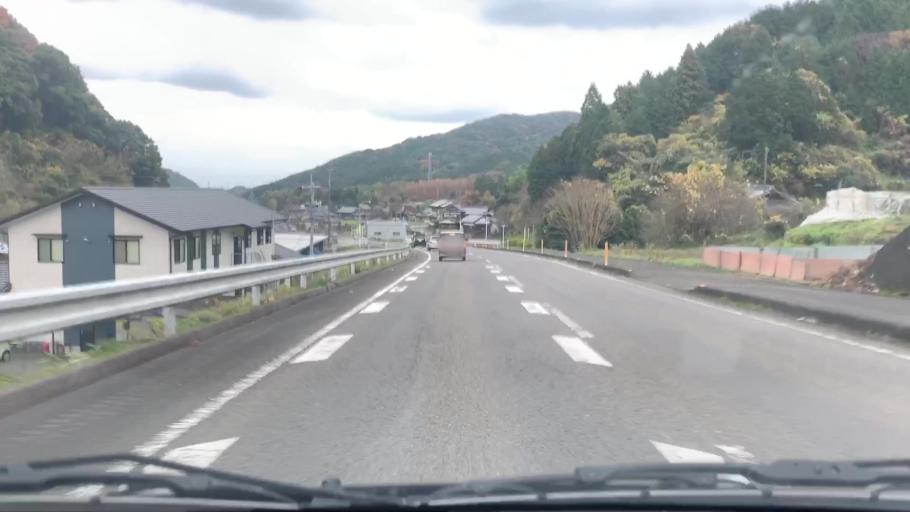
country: JP
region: Saga Prefecture
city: Kashima
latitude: 33.0986
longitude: 130.0481
